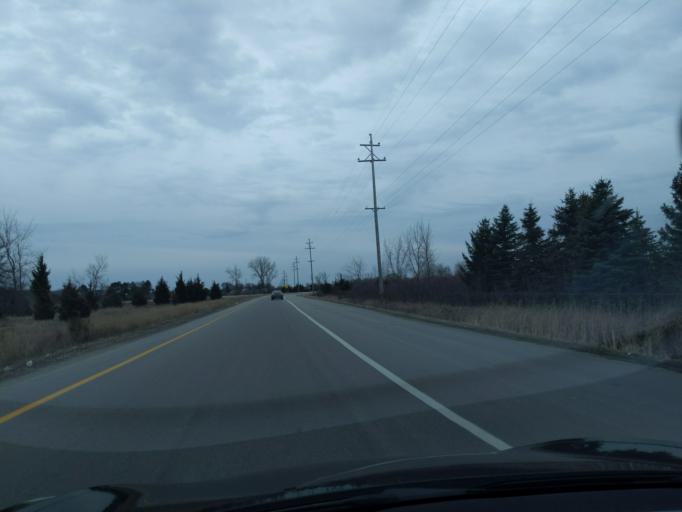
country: US
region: Michigan
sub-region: Bay County
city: Bay City
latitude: 43.6235
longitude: -83.9466
